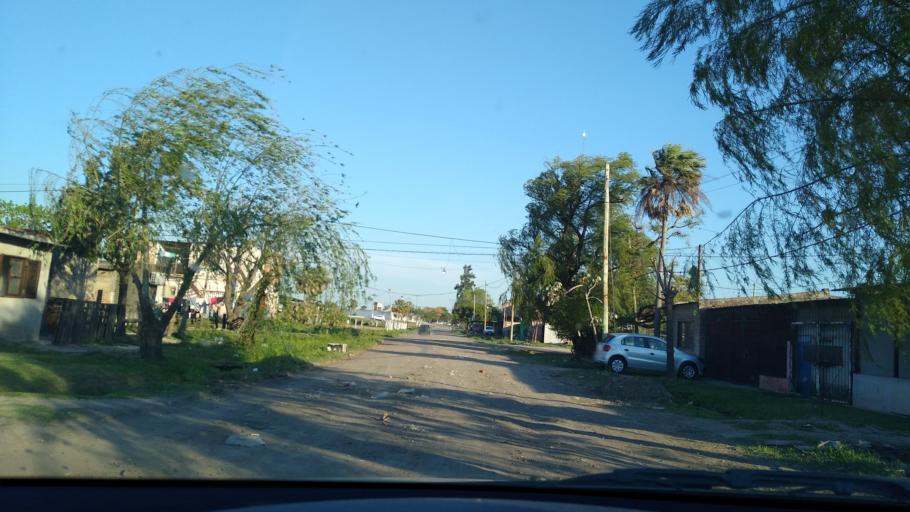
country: AR
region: Chaco
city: Puerto Vilelas
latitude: -27.5146
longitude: -58.9437
